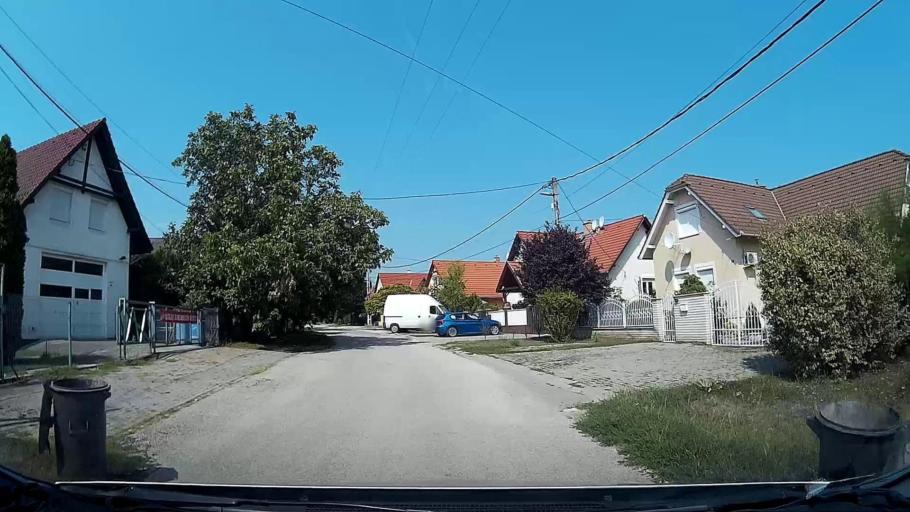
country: HU
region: Pest
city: Szentendre
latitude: 47.6868
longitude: 19.0496
